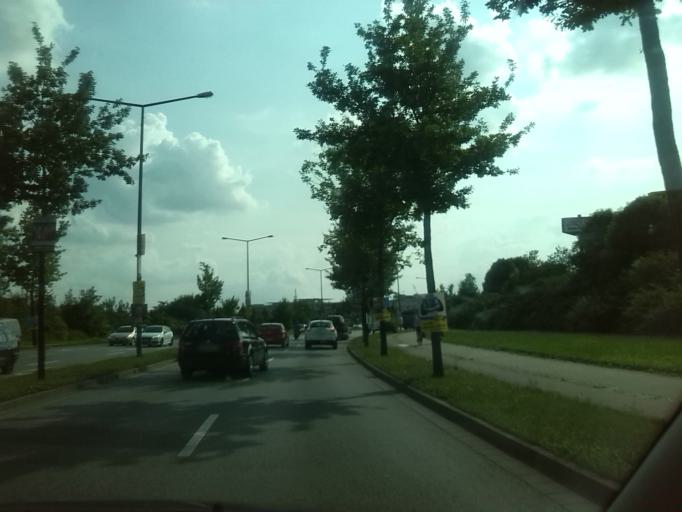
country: DE
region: Saxony
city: Radebeul
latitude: 51.0800
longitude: 13.6926
